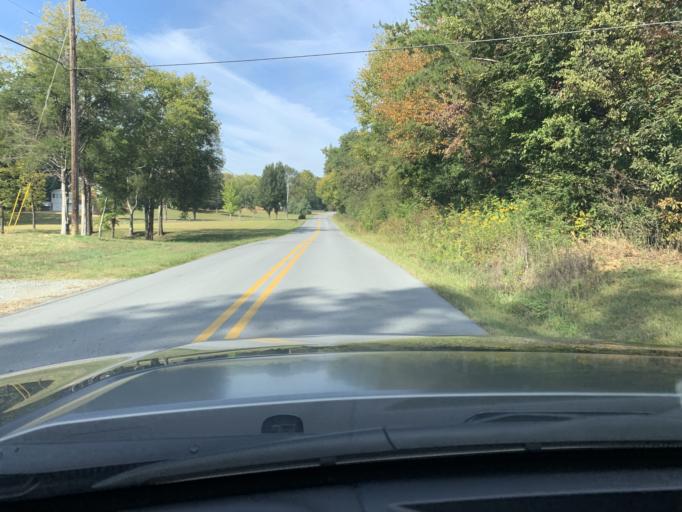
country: US
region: Georgia
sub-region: Polk County
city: Rockmart
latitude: 34.0318
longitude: -85.0219
